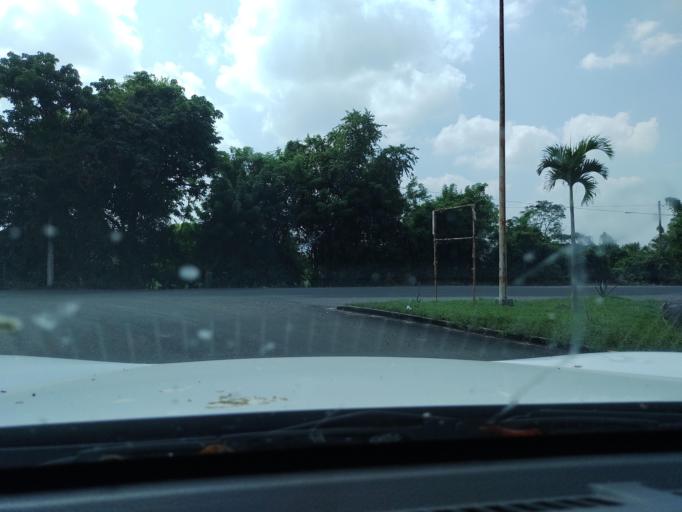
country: MX
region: Veracruz
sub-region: Atzalan
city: Colonias Pedernales
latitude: 20.0588
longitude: -97.0311
